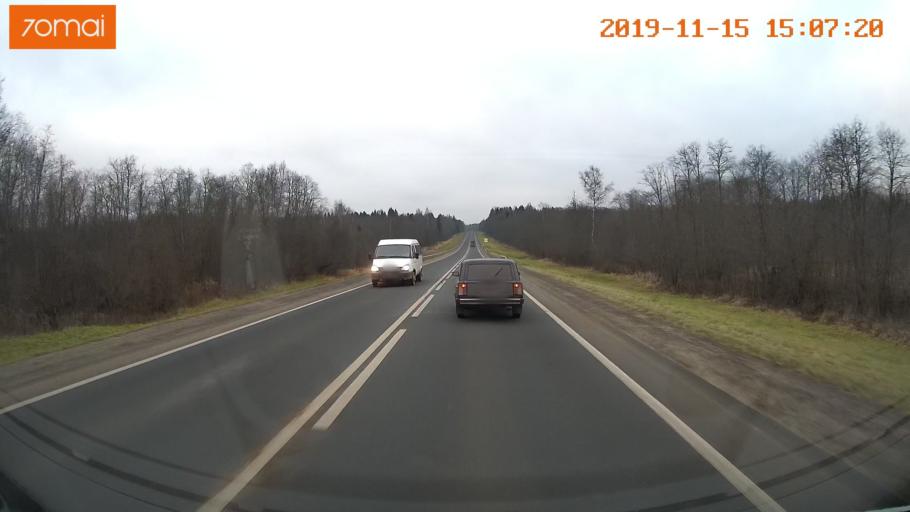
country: RU
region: Jaroslavl
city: Prechistoye
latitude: 58.3849
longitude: 40.2976
